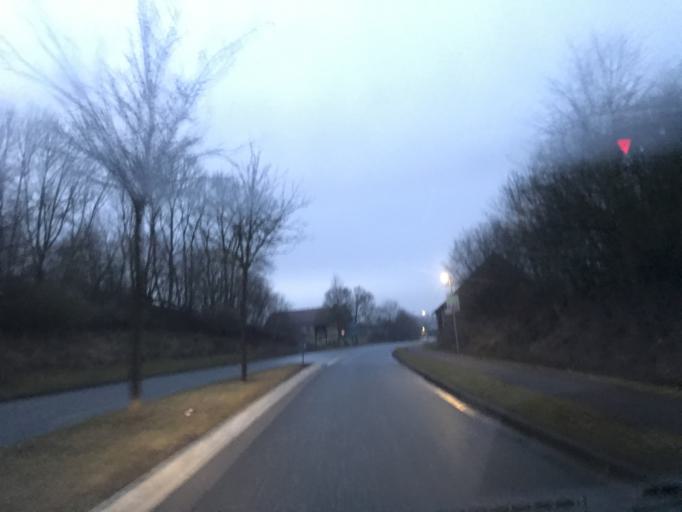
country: DE
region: Hesse
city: Trendelburg
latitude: 51.5632
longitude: 9.4170
